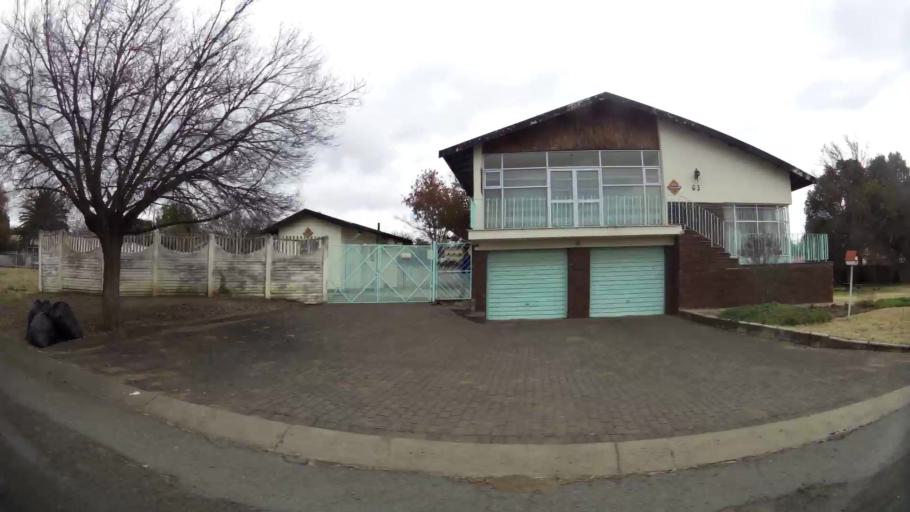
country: ZA
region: Orange Free State
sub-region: Fezile Dabi District Municipality
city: Kroonstad
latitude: -27.6834
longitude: 27.2404
